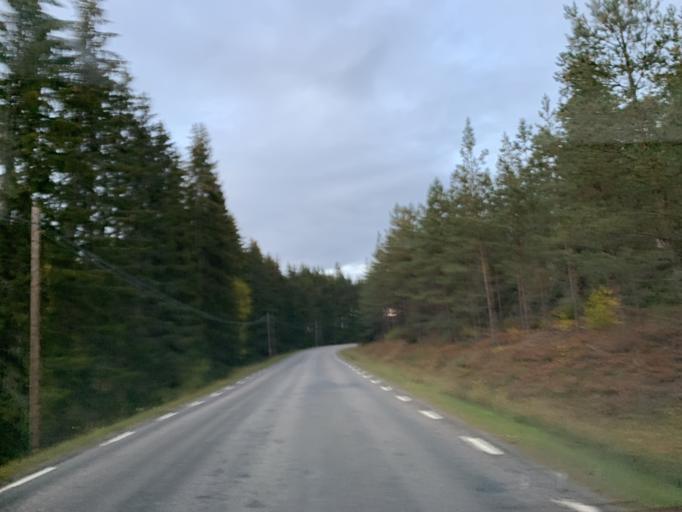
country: SE
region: Stockholm
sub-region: Nynashamns Kommun
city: Osmo
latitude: 58.9391
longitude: 17.7577
